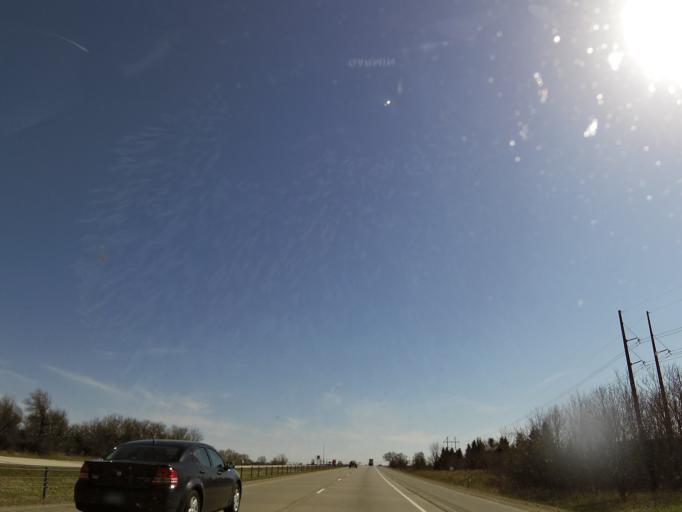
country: US
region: Minnesota
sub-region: Dakota County
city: Lakeville
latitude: 44.6566
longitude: -93.2943
